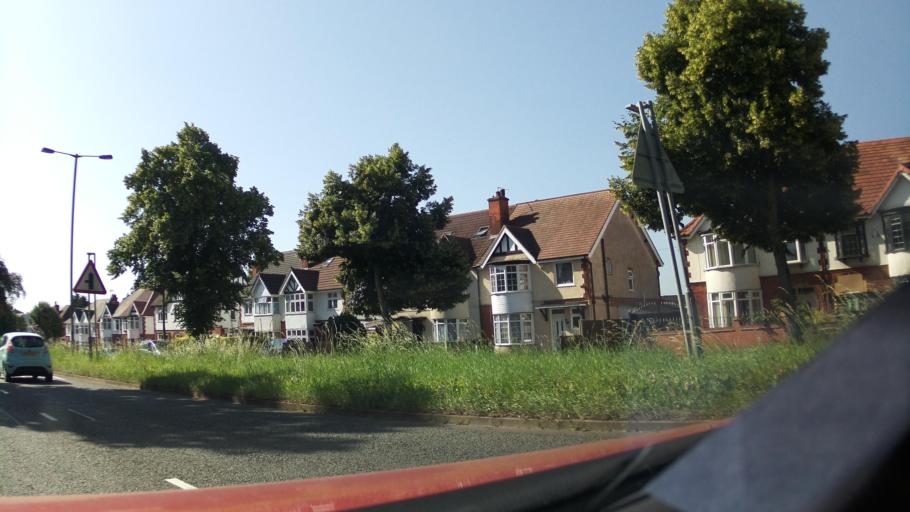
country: GB
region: England
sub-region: Derby
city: Derby
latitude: 52.9044
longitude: -1.4971
